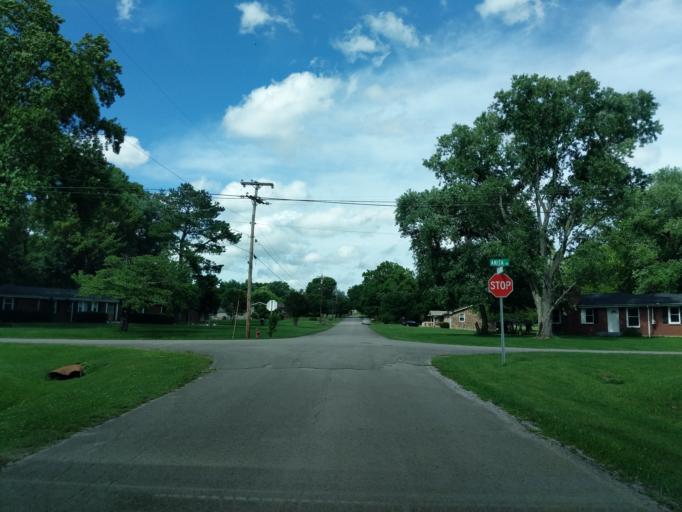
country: US
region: Tennessee
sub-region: Davidson County
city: Lakewood
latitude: 36.2612
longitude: -86.6659
